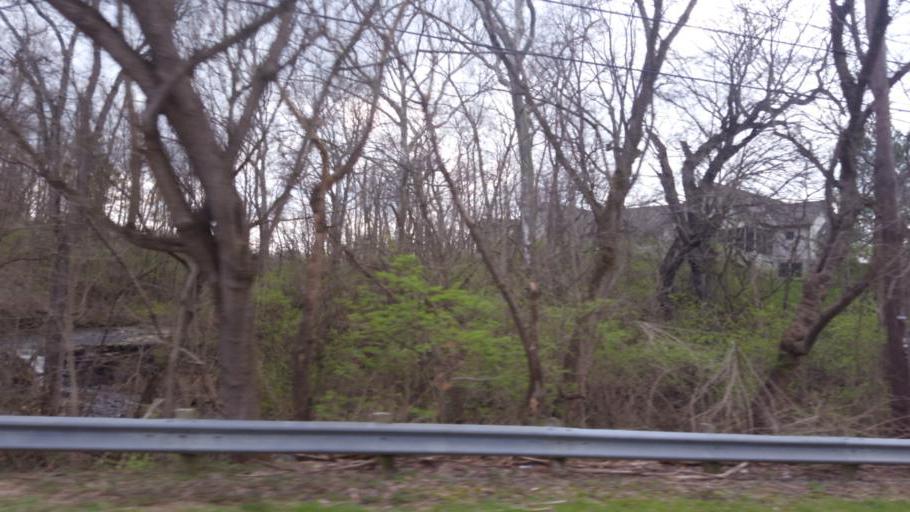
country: US
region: Ohio
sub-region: Delaware County
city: Delaware
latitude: 40.2697
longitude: -83.0661
